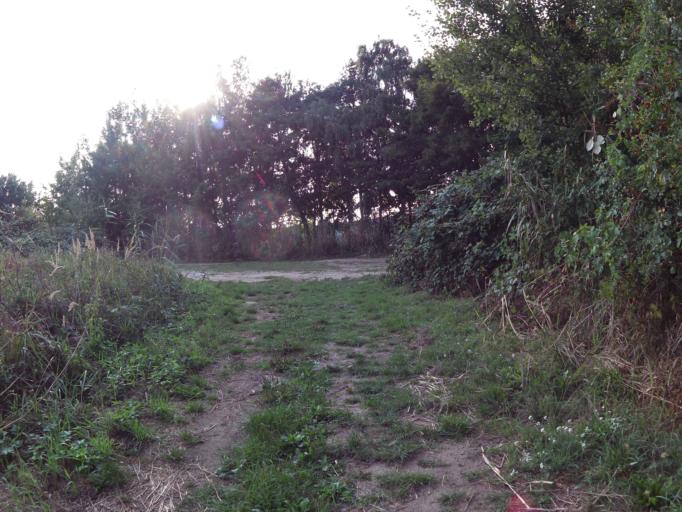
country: DE
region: Mecklenburg-Vorpommern
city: Seebad Bansin
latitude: 53.9651
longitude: 14.1480
